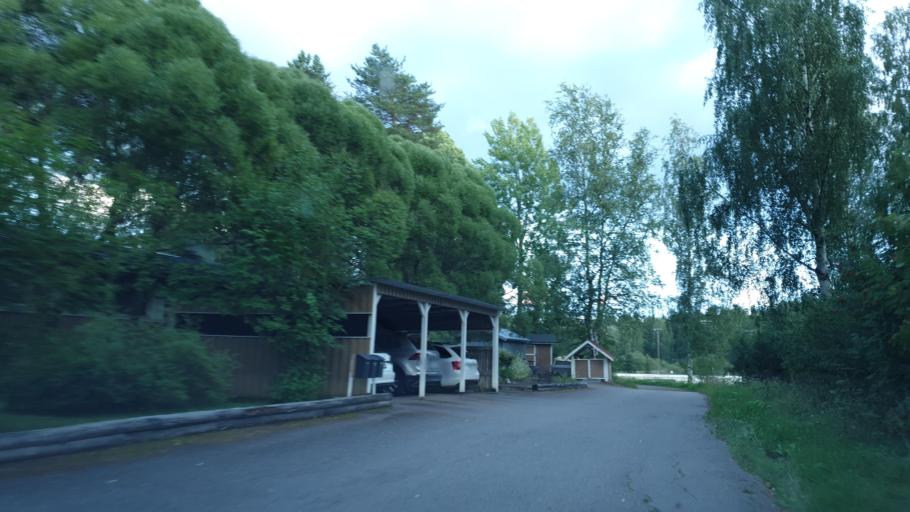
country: FI
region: Northern Savo
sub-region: Varkaus
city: Leppaevirta
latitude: 62.5873
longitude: 27.6099
